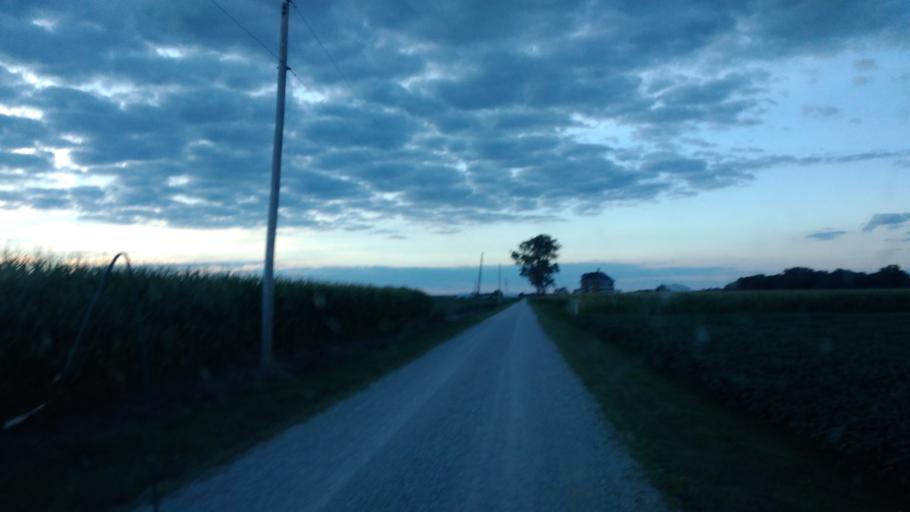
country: US
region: Indiana
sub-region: Adams County
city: Berne
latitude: 40.6440
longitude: -85.0796
